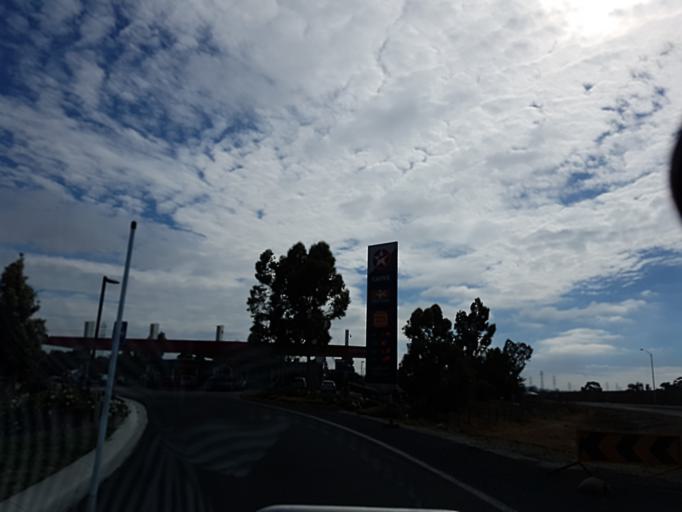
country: AU
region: Victoria
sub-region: Cardinia
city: Bunyip
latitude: -38.0860
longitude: 145.7742
